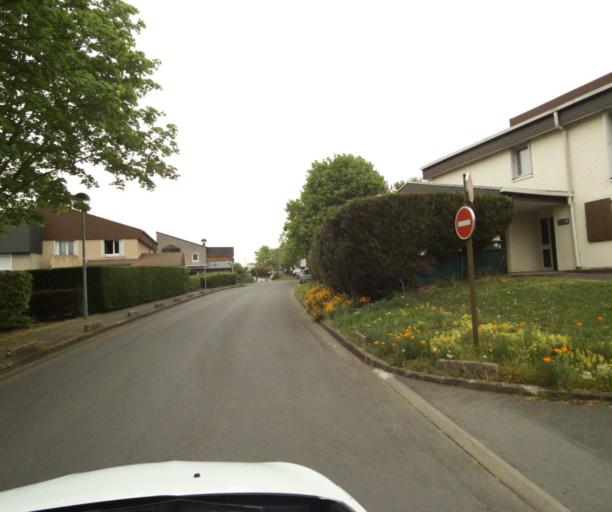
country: FR
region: Ile-de-France
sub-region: Departement de Seine-et-Marne
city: Noisiel
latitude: 48.8494
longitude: 2.6342
